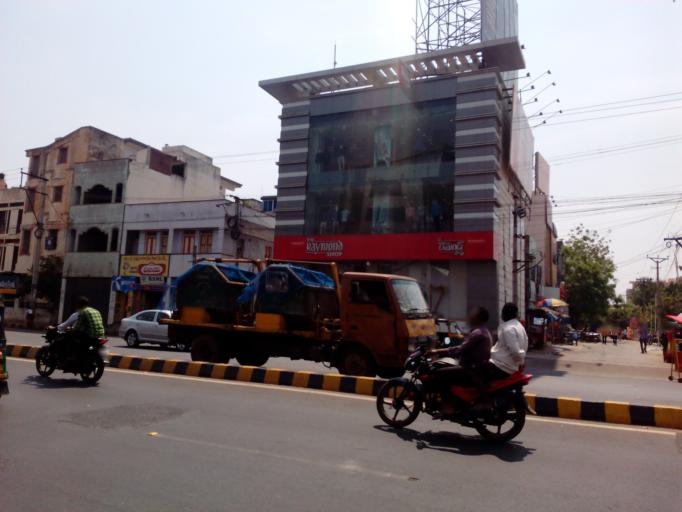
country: IN
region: Andhra Pradesh
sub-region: Krishna
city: Vijayawada
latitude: 16.5011
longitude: 80.6450
